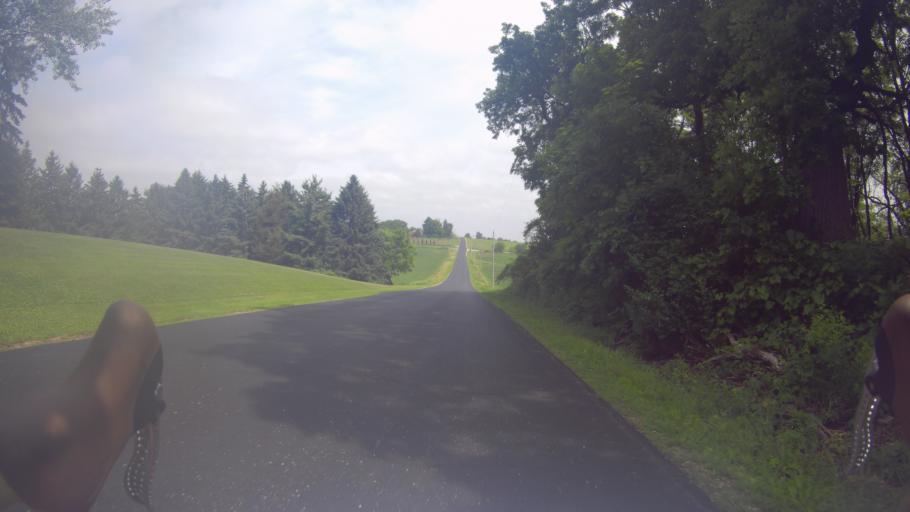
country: US
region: Wisconsin
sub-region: Rock County
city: Edgerton
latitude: 42.9022
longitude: -89.0427
